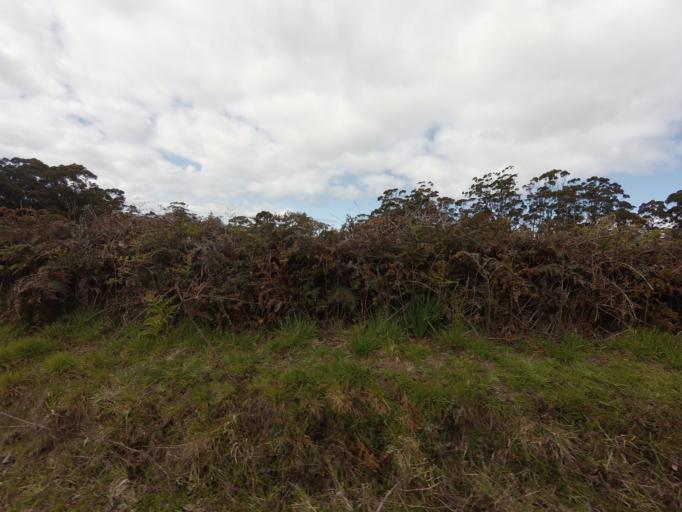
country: AU
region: Tasmania
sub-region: Huon Valley
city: Cygnet
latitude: -43.4127
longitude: 147.0182
